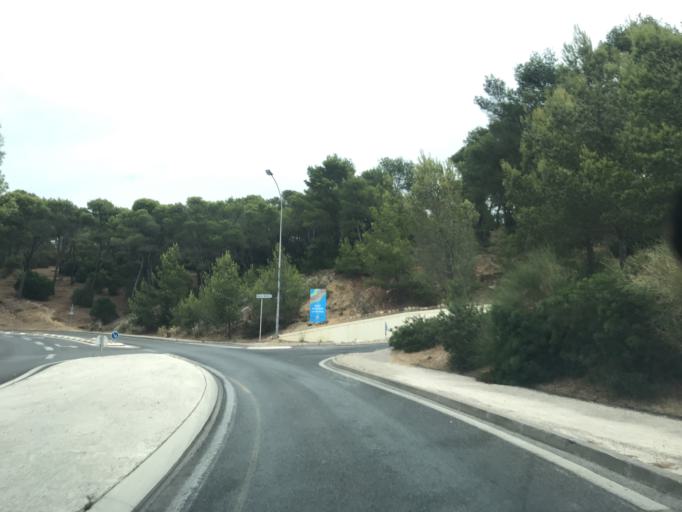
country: FR
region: Provence-Alpes-Cote d'Azur
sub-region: Departement du Var
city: Saint-Mandrier-sur-Mer
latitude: 43.0783
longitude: 5.9115
